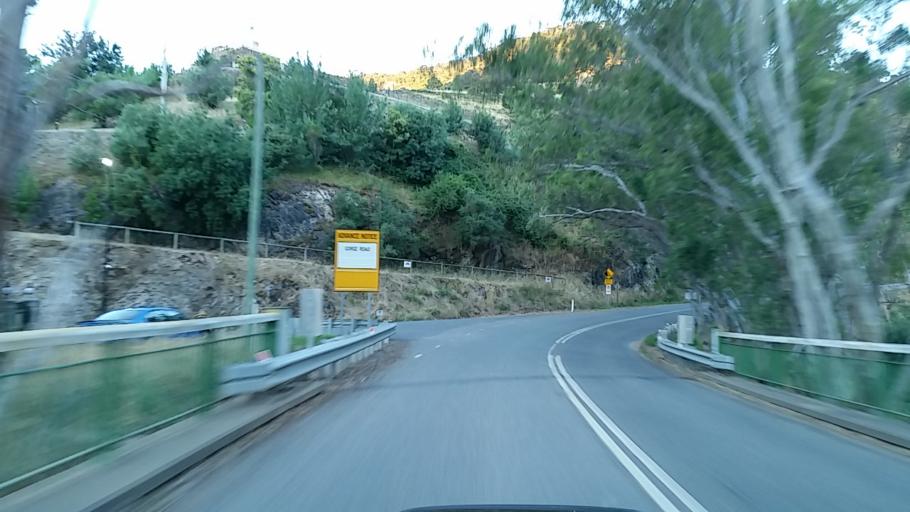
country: AU
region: South Australia
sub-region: Campbelltown
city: Athelstone
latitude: -34.8651
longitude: 138.7583
